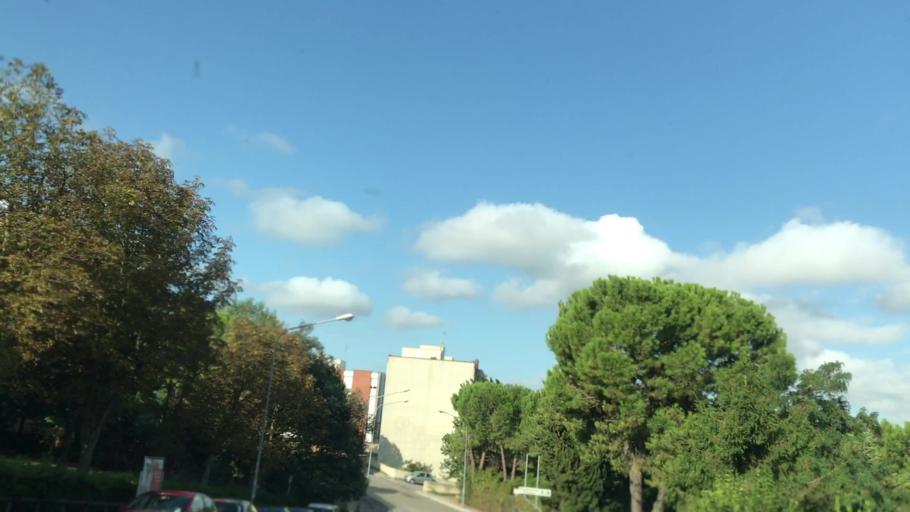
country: IT
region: The Marches
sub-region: Provincia di Ancona
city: Le Grazie di Ancona
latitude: 43.5925
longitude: 13.5147
